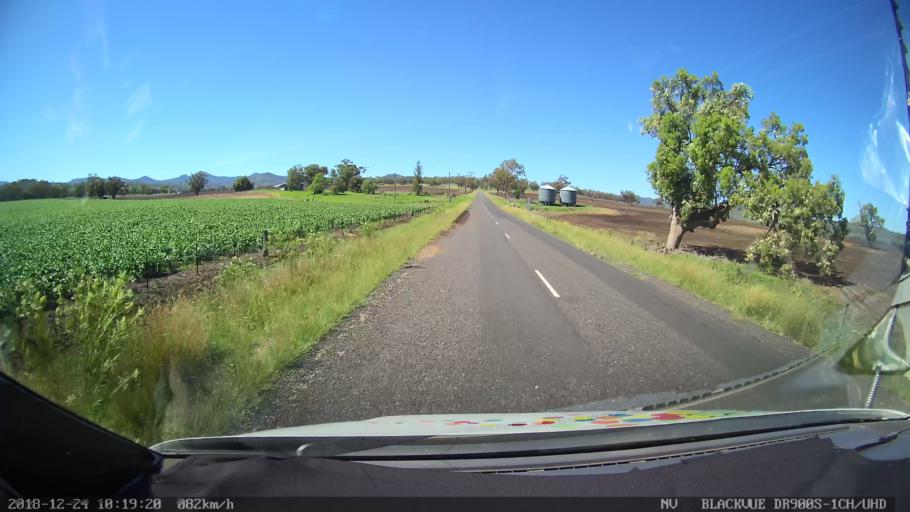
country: AU
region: New South Wales
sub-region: Liverpool Plains
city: Quirindi
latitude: -31.7292
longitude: 150.5656
